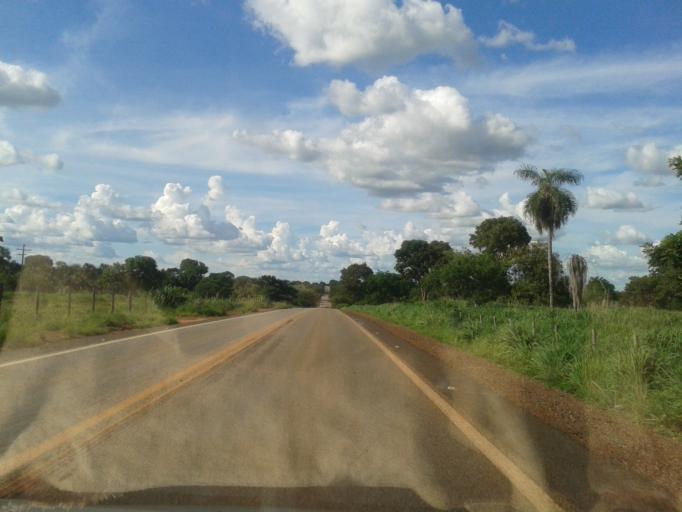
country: BR
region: Goias
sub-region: Mozarlandia
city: Mozarlandia
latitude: -14.7442
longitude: -50.5426
